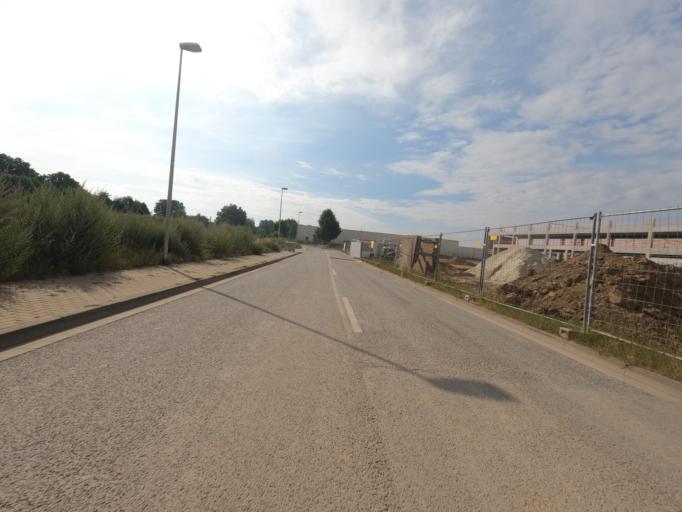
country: DE
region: North Rhine-Westphalia
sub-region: Regierungsbezirk Koln
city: Heinsberg
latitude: 51.0604
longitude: 6.1291
